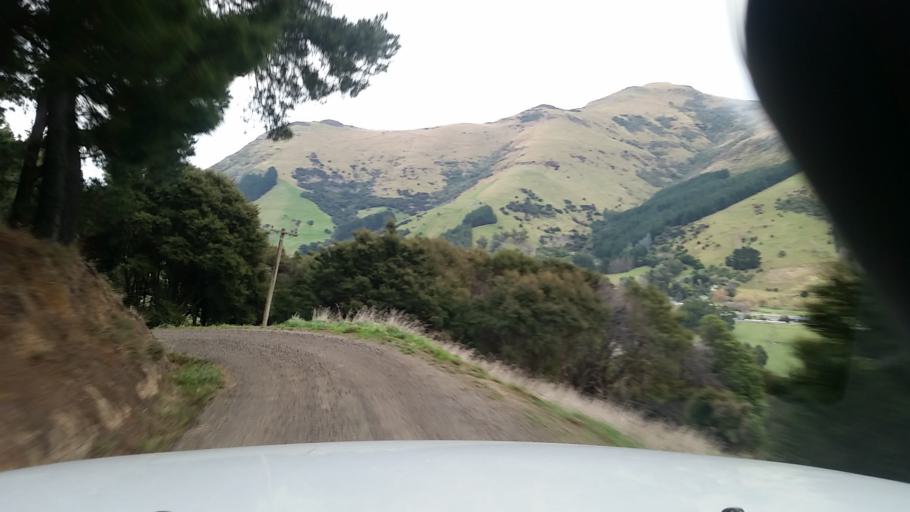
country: NZ
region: Canterbury
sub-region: Christchurch City
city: Christchurch
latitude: -43.7747
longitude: 172.8001
